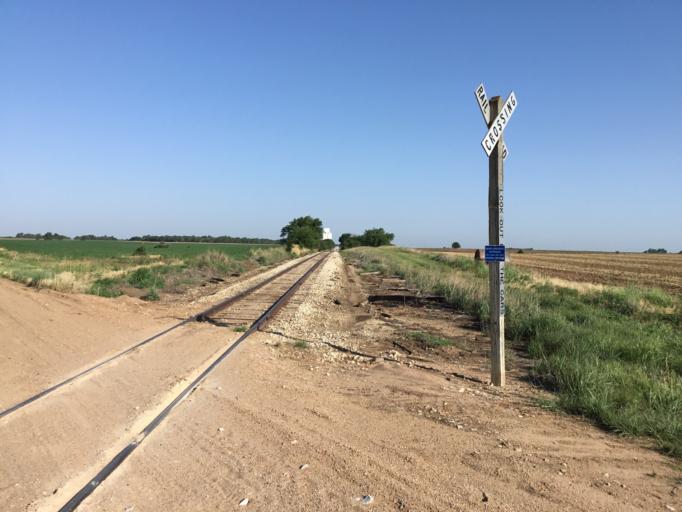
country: US
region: Kansas
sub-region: Kingman County
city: Kingman
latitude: 37.5176
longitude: -97.9737
